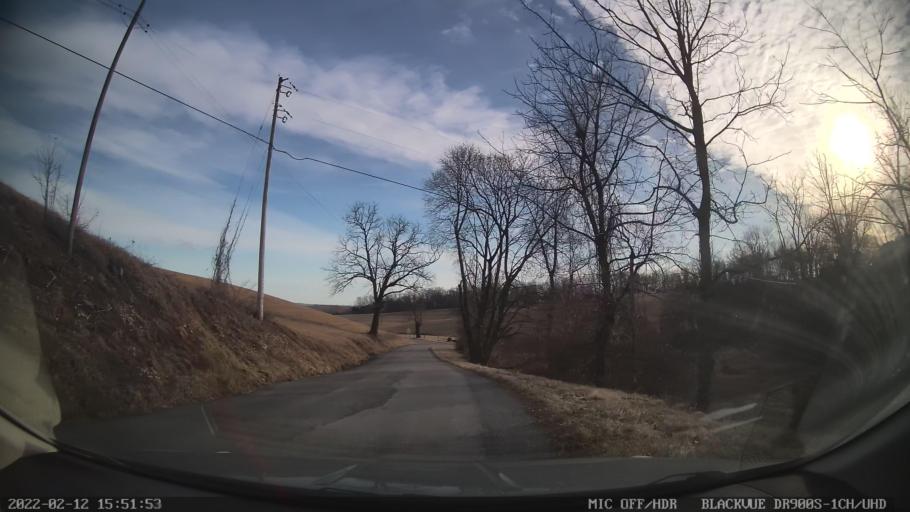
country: US
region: Pennsylvania
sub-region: Berks County
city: Kutztown
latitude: 40.5736
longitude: -75.7685
